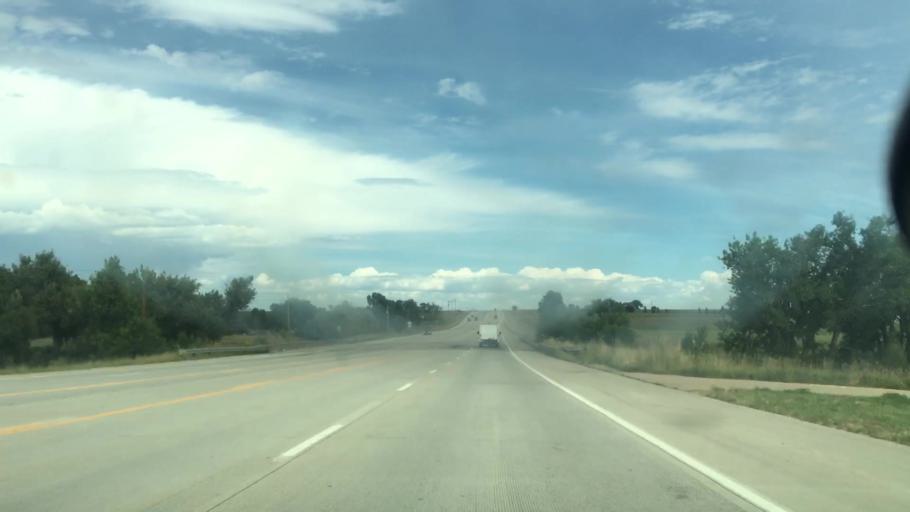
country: US
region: Colorado
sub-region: Larimer County
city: Berthoud
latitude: 40.2765
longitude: -105.1024
